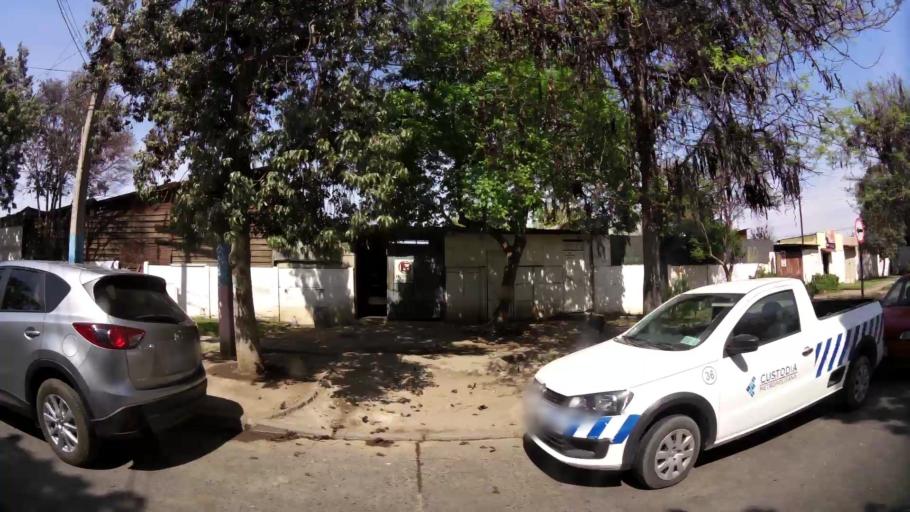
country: CL
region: Santiago Metropolitan
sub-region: Provincia de Santiago
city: Lo Prado
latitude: -33.4349
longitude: -70.7295
